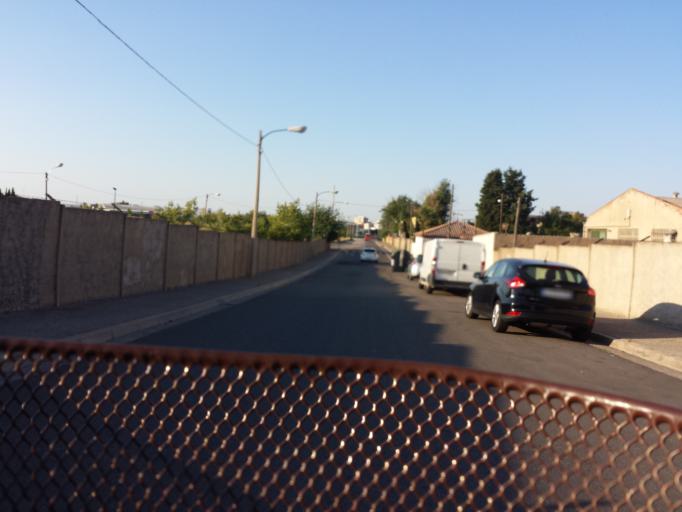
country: ES
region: Aragon
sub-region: Provincia de Zaragoza
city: Oliver-Valdefierro, Oliver, Valdefierro
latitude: 41.6425
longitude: -0.9278
